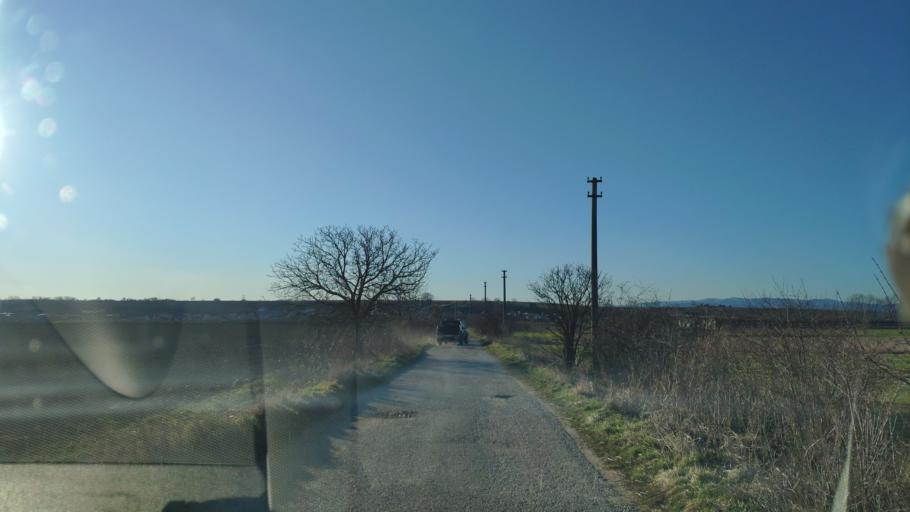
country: HU
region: Borsod-Abauj-Zemplen
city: Gonc
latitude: 48.5889
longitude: 21.3156
